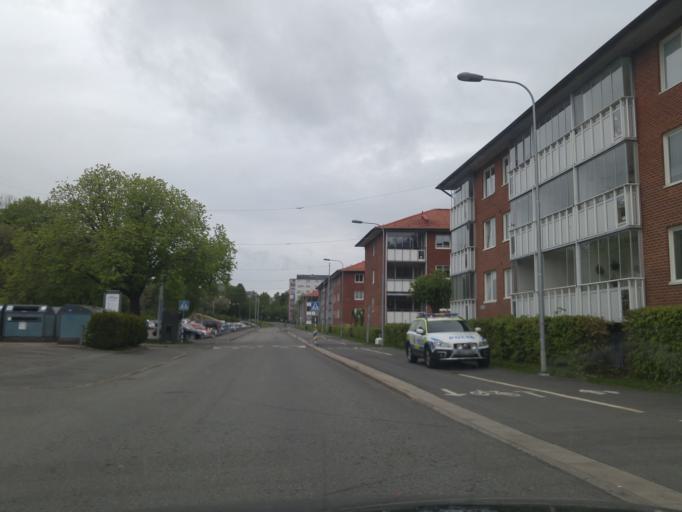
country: SE
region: Vaestra Goetaland
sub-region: Goteborg
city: Majorna
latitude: 57.6695
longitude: 11.9315
